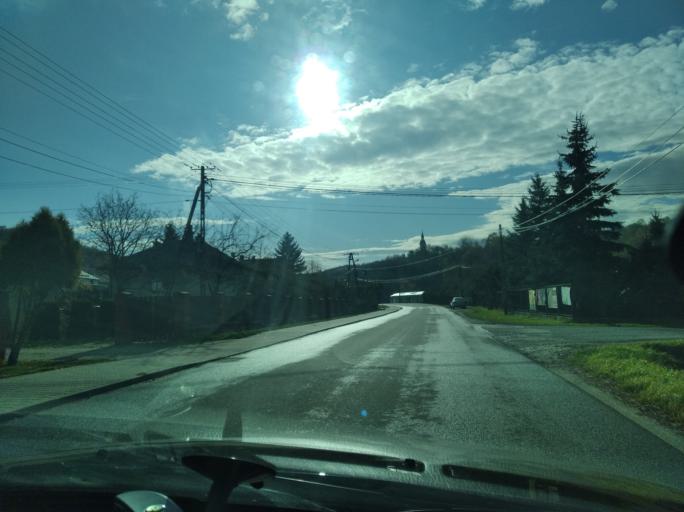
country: PL
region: Subcarpathian Voivodeship
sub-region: Powiat debicki
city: Brzeznica
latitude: 50.0534
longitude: 21.4842
